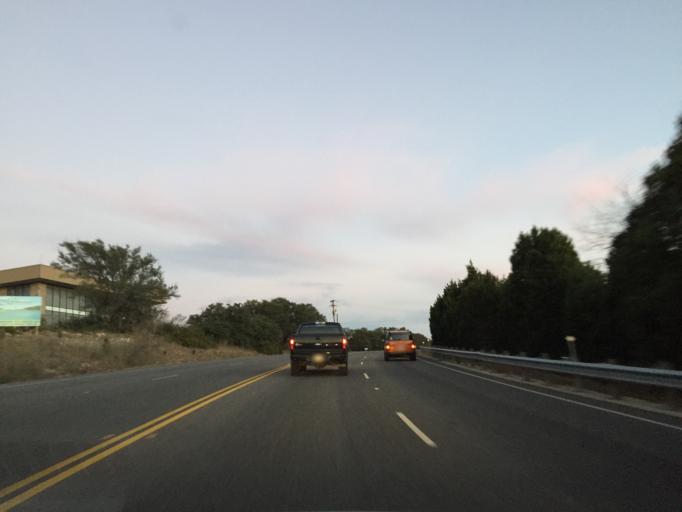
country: US
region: Texas
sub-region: Travis County
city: Jonestown
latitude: 30.5177
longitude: -97.8904
